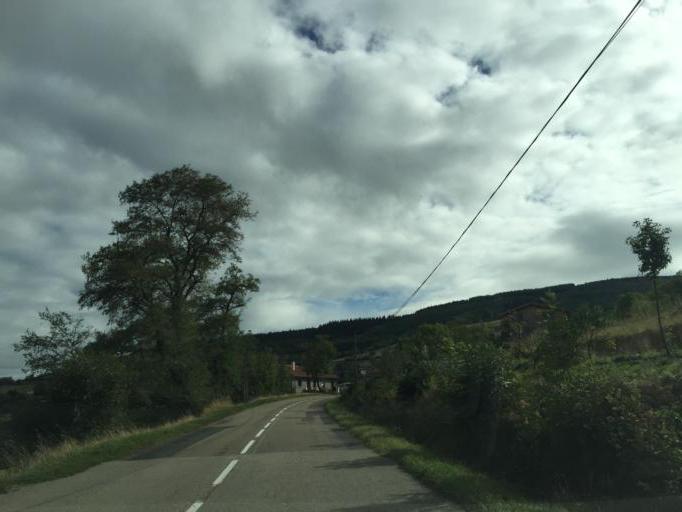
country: FR
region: Rhone-Alpes
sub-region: Departement de la Loire
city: Farnay
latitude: 45.4514
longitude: 4.6097
